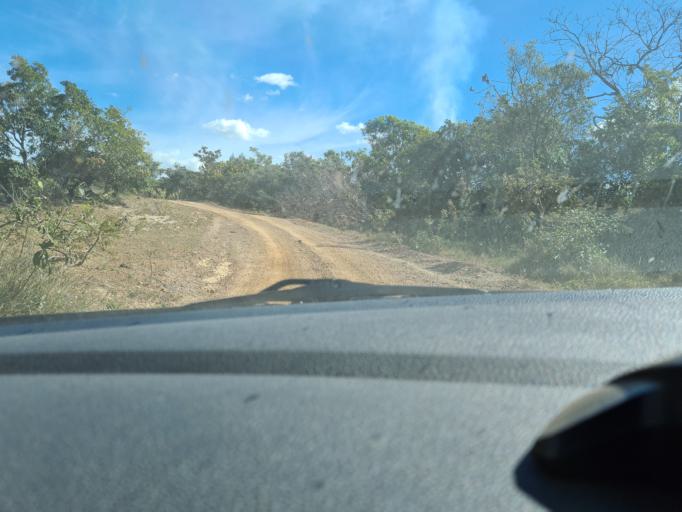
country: BR
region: Goias
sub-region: Silvania
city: Silvania
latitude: -16.5274
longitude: -48.5398
